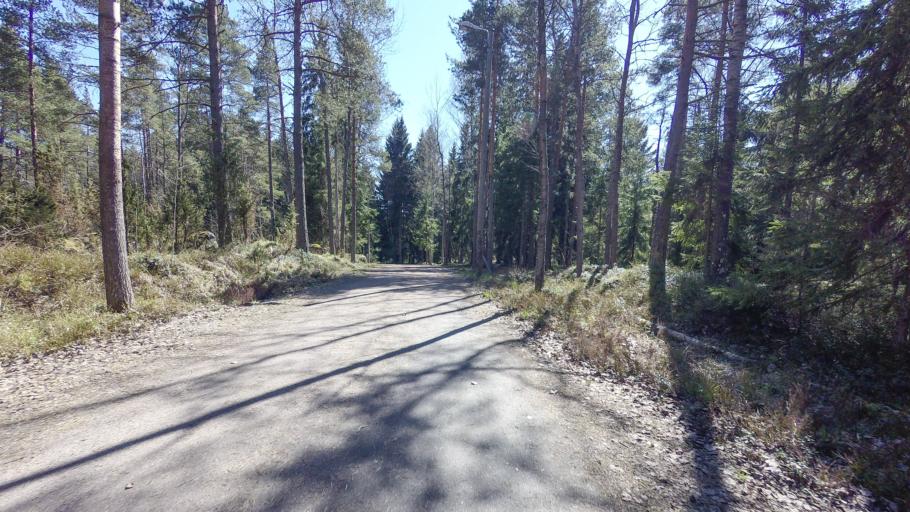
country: FI
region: Uusimaa
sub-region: Helsinki
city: Vantaa
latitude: 60.2318
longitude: 25.1425
